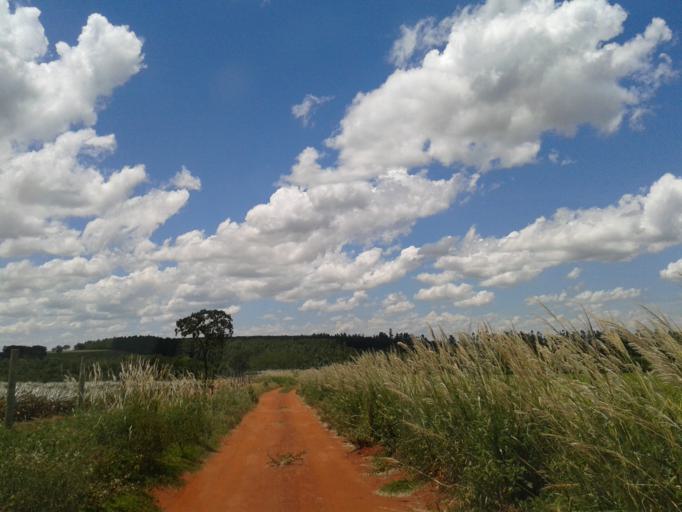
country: BR
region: Minas Gerais
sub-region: Centralina
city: Centralina
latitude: -18.6977
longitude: -49.1646
